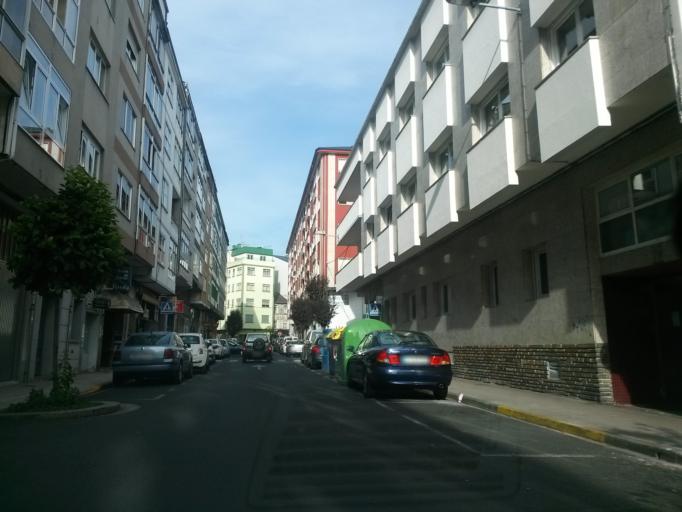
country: ES
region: Galicia
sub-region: Provincia de Lugo
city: Lugo
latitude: 43.0174
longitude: -7.5654
